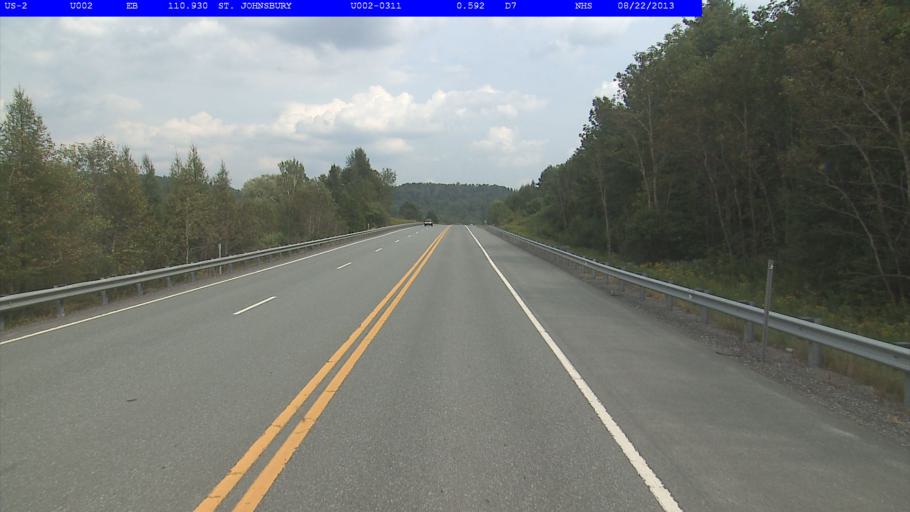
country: US
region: Vermont
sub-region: Caledonia County
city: St Johnsbury
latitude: 44.4435
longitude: -72.0495
